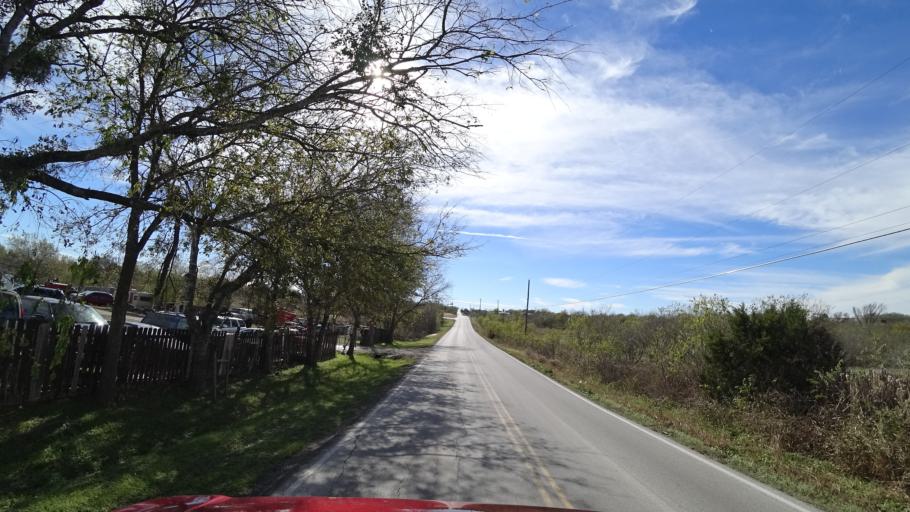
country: US
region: Texas
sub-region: Travis County
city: Onion Creek
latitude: 30.1257
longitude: -97.7399
